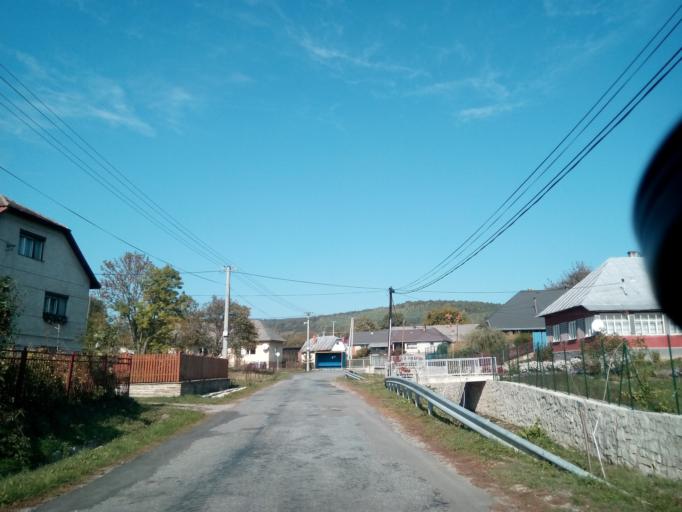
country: SK
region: Presovsky
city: Svidnik
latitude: 49.3912
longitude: 21.4936
